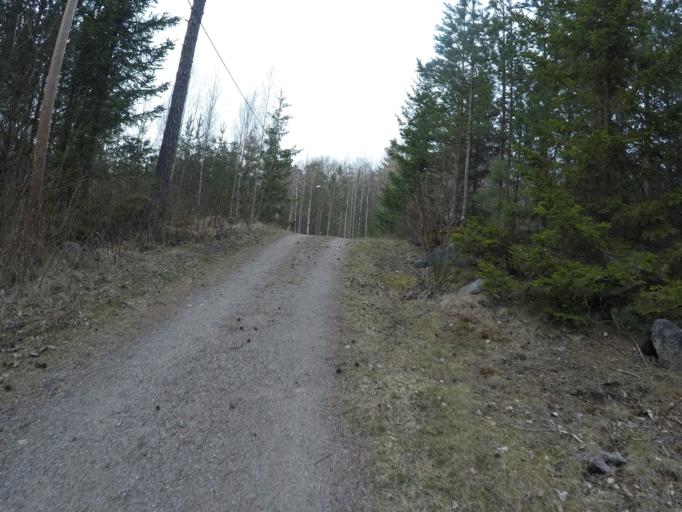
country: SE
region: Soedermanland
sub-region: Eskilstuna Kommun
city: Torshalla
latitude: 59.4220
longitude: 16.5000
